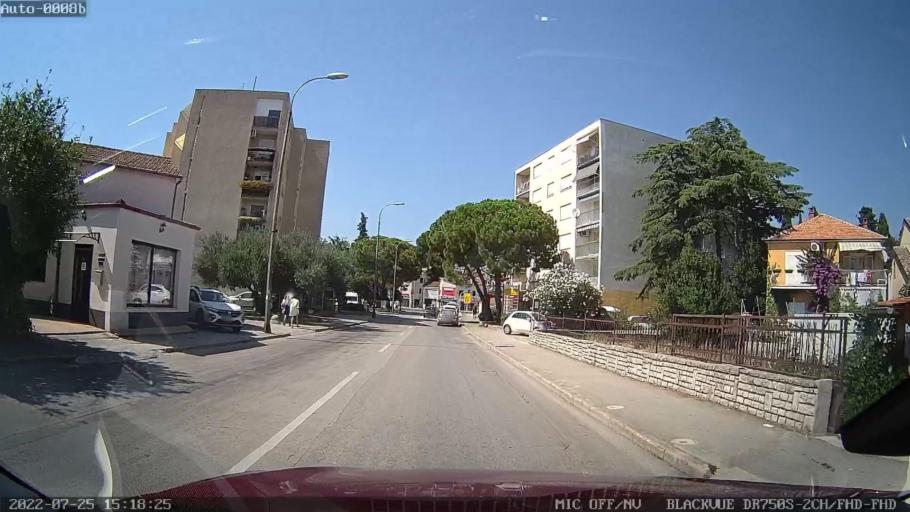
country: HR
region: Zadarska
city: Biograd na Moru
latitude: 43.9362
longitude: 15.4453
